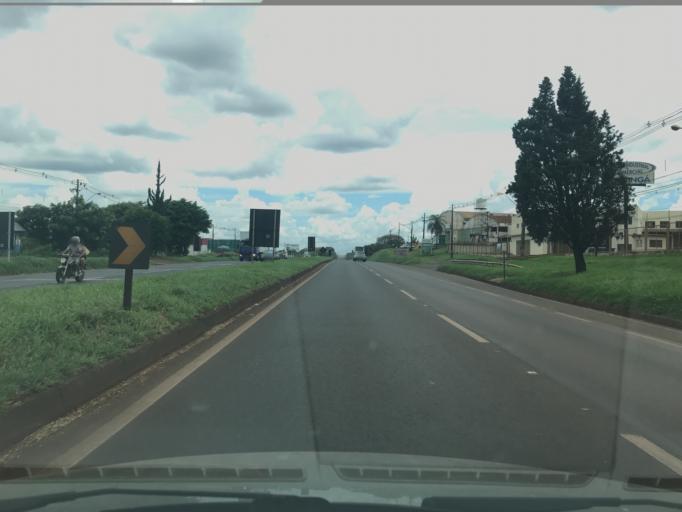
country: BR
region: Parana
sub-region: Maringa
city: Maringa
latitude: -23.4378
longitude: -51.9781
